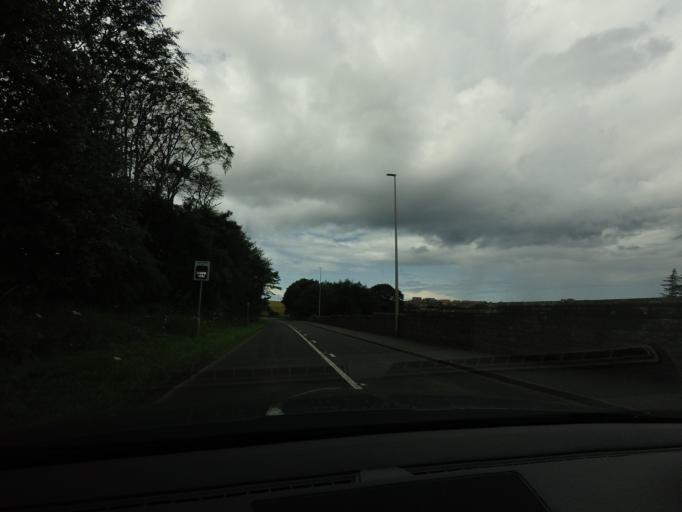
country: GB
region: Scotland
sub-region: Aberdeenshire
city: Macduff
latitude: 57.6596
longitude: -2.4914
